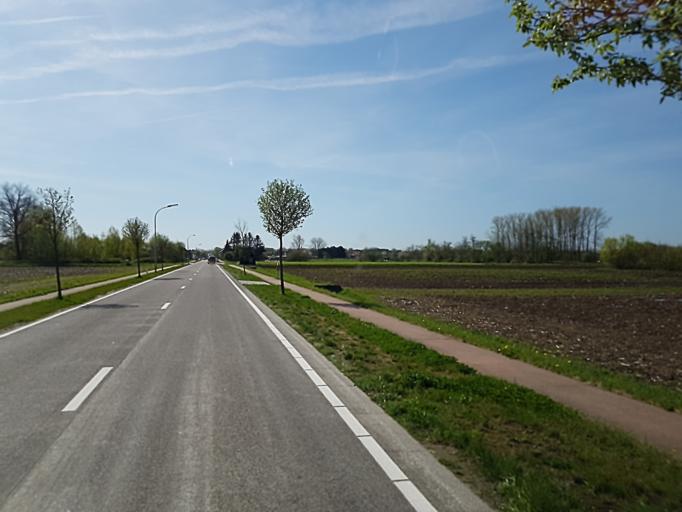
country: BE
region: Flanders
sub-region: Provincie Antwerpen
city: Westerlo
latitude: 51.1079
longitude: 4.9439
